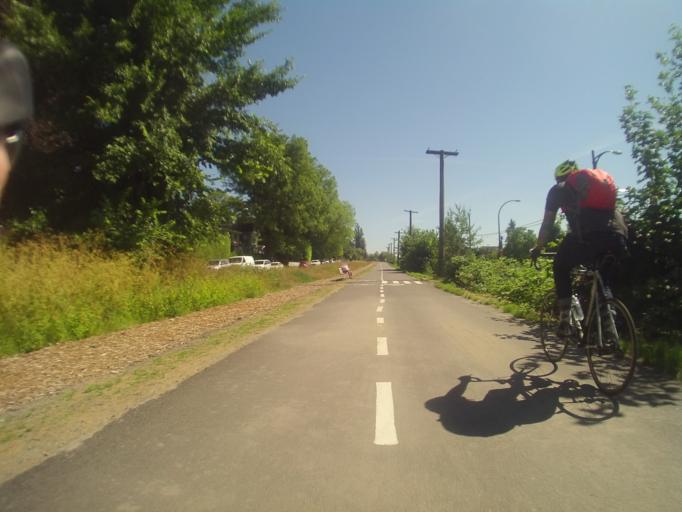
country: CA
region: British Columbia
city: Vancouver
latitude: 49.2548
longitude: -123.1528
